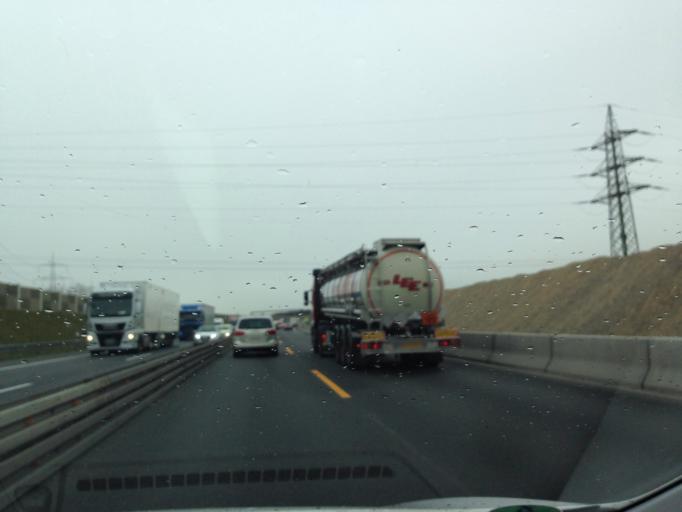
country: DE
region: North Rhine-Westphalia
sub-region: Regierungsbezirk Dusseldorf
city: Kaarst
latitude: 51.2229
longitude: 6.6396
